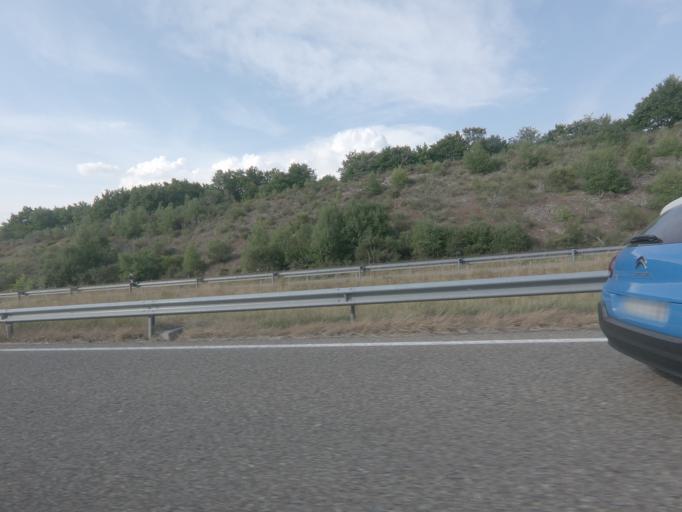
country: ES
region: Galicia
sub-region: Provincia de Ourense
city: Xinzo de Limia
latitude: 42.0671
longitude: -7.7025
